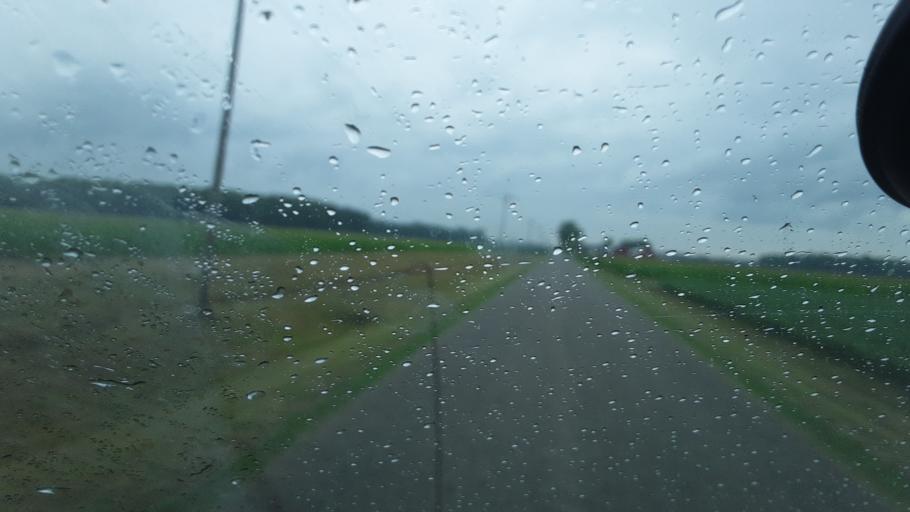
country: US
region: Ohio
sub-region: Defiance County
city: Hicksville
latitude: 41.3082
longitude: -84.6695
